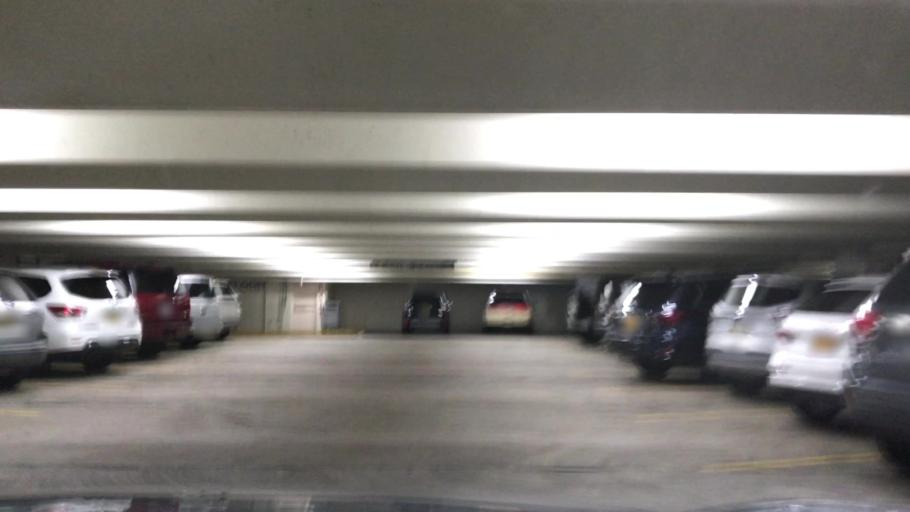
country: US
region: New Jersey
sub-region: Atlantic County
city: Atlantic City
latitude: 39.3577
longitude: -74.4360
